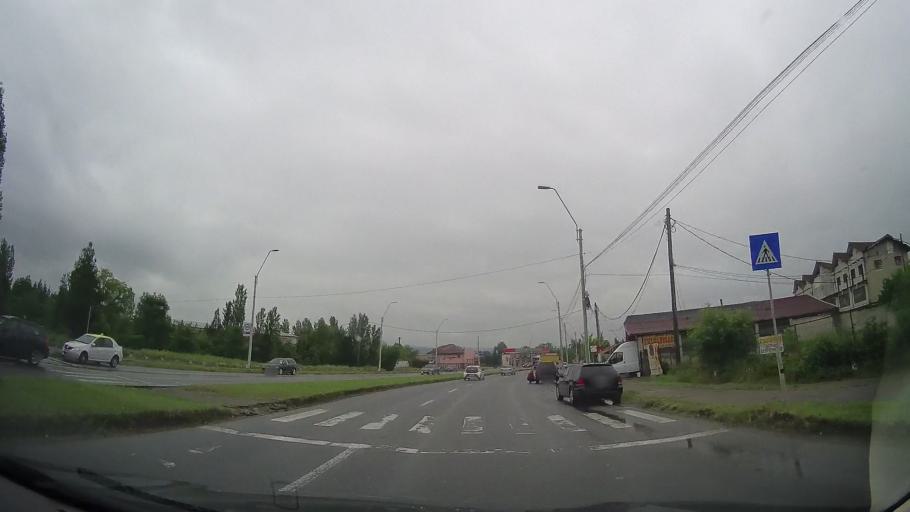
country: RO
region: Mehedinti
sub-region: Comuna Simian
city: Dudasu
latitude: 44.6321
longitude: 22.6832
